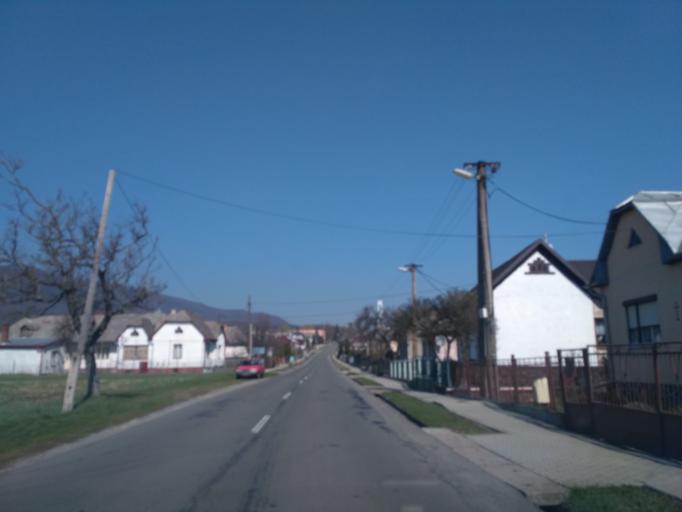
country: SK
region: Kosicky
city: Secovce
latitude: 48.7556
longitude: 21.6431
